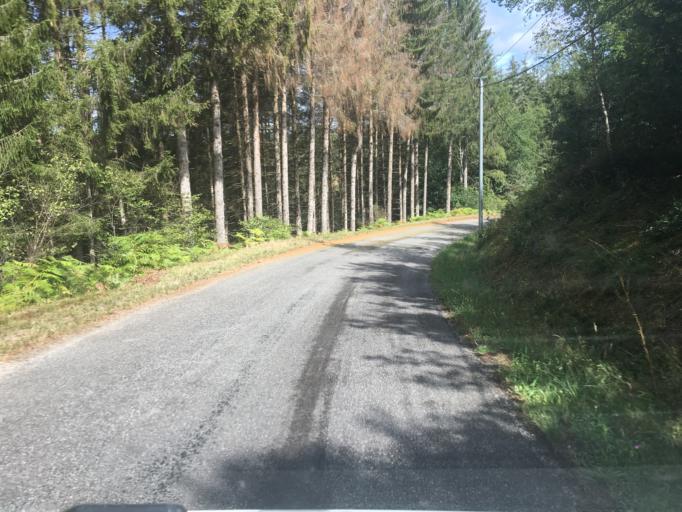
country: FR
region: Auvergne
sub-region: Departement du Cantal
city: Champagnac
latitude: 45.4221
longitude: 2.4060
